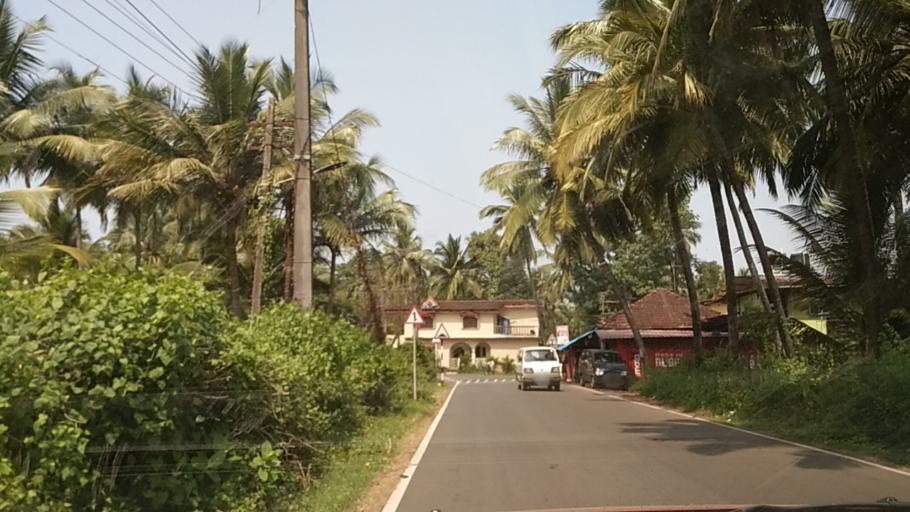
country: IN
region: Goa
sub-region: South Goa
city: Colva
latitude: 15.3135
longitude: 73.9144
